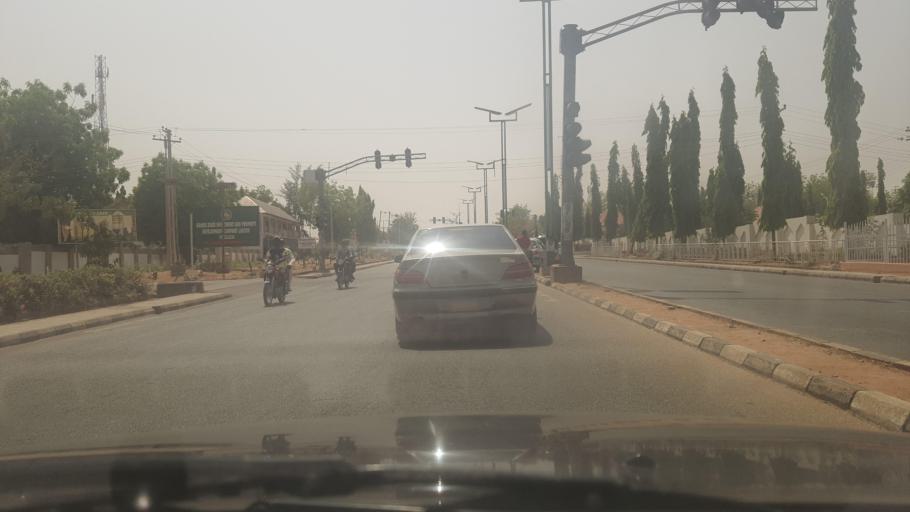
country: NG
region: Gombe
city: Gombe
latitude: 10.2846
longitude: 11.1478
